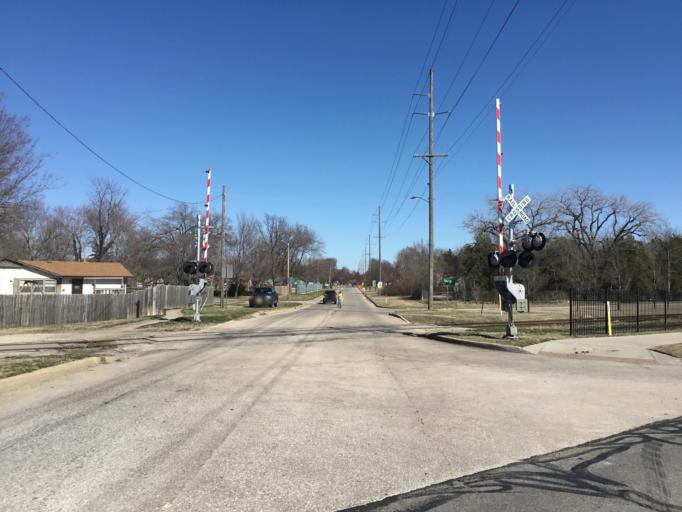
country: US
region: Kansas
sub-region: Sedgwick County
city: Wichita
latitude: 37.7016
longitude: -97.3868
